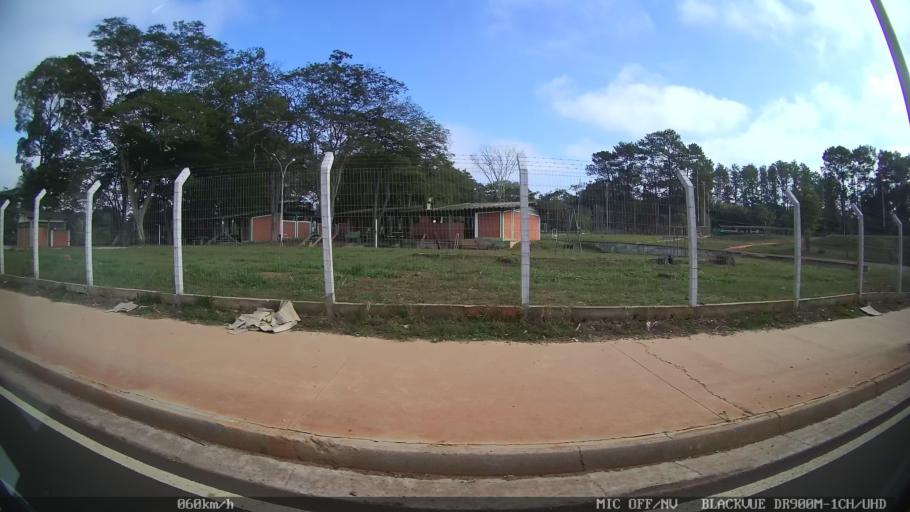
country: BR
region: Sao Paulo
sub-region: Sao Jose Do Rio Preto
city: Sao Jose do Rio Preto
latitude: -20.8116
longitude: -49.4332
